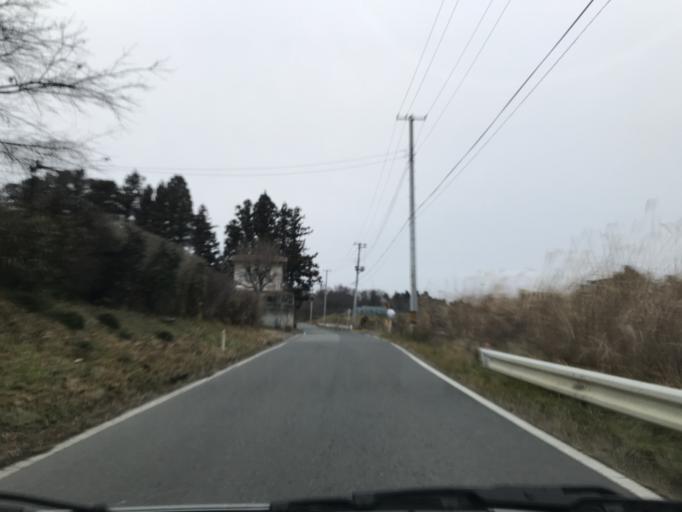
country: JP
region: Miyagi
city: Kogota
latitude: 38.6911
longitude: 141.0954
